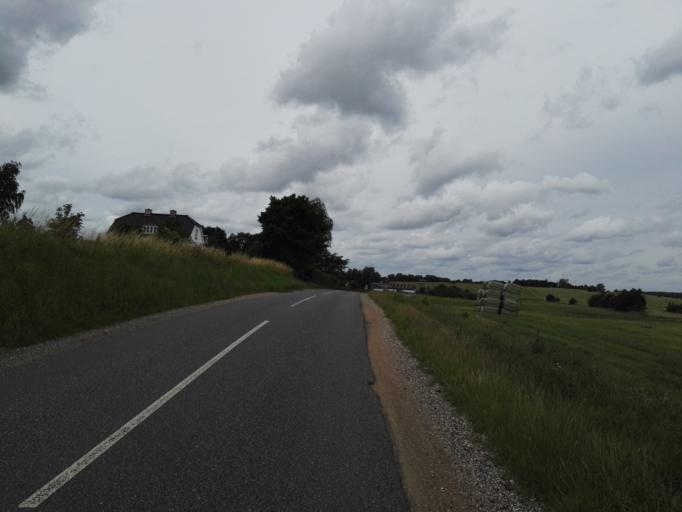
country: DK
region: Capital Region
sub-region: Egedal Kommune
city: Stenlose
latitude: 55.7820
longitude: 12.2046
